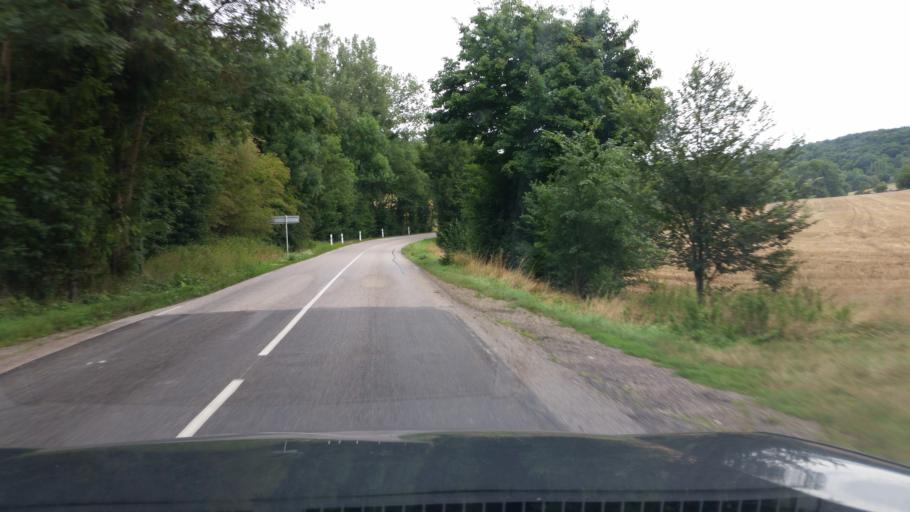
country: FR
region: Lorraine
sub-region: Departement de Meurthe-et-Moselle
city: Marbache
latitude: 48.7966
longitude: 6.0803
